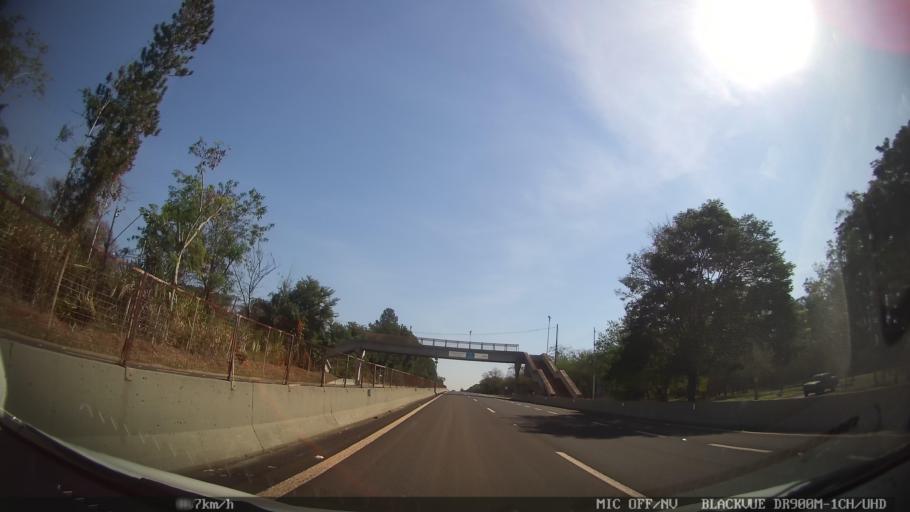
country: BR
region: Sao Paulo
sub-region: Ribeirao Preto
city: Ribeirao Preto
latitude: -21.1732
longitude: -47.8596
